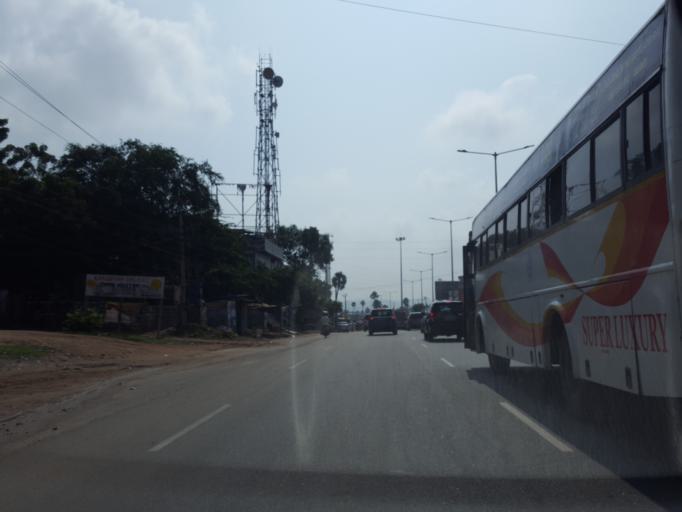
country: IN
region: Telangana
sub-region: Rangareddi
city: Lal Bahadur Nagar
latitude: 17.3107
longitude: 78.6850
